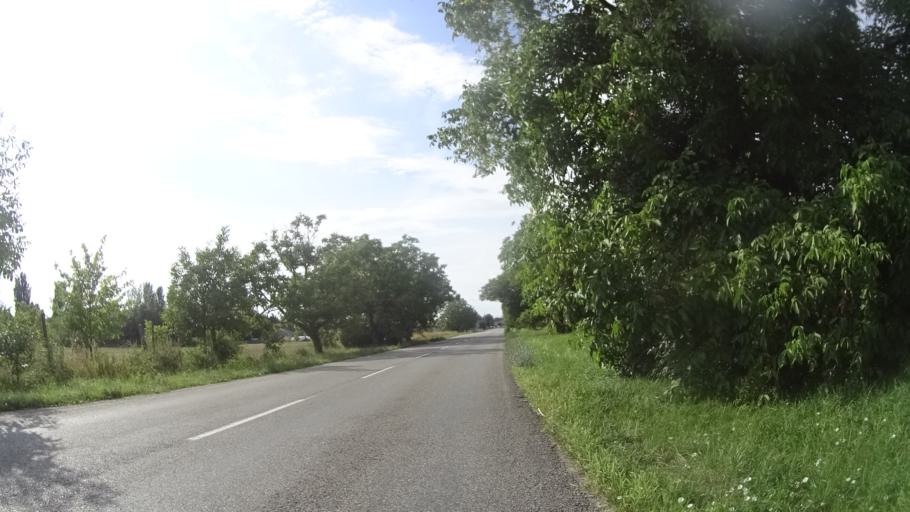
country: SK
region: Trnavsky
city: Gabcikovo
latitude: 47.9155
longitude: 17.5069
